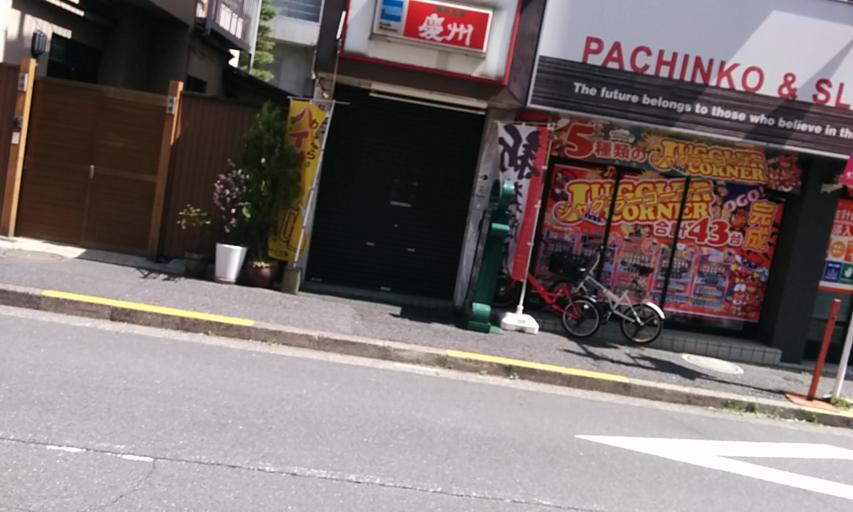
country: JP
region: Tokyo
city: Tokyo
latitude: 35.7067
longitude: 139.6863
